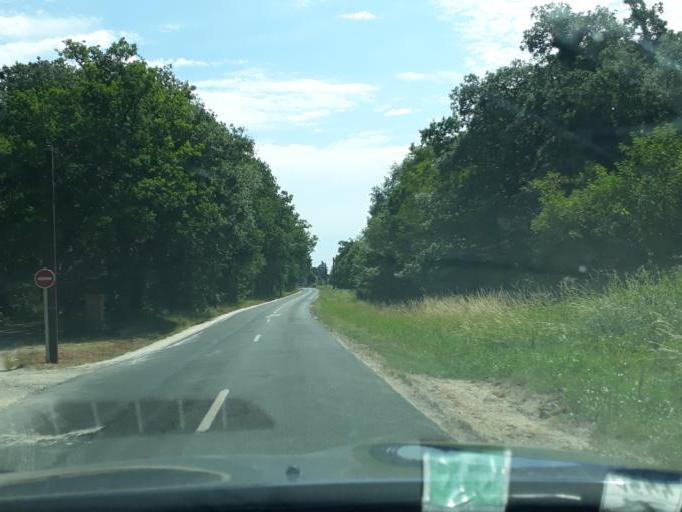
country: FR
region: Centre
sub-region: Departement du Loir-et-Cher
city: Vouzon
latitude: 47.6455
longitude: 2.0435
